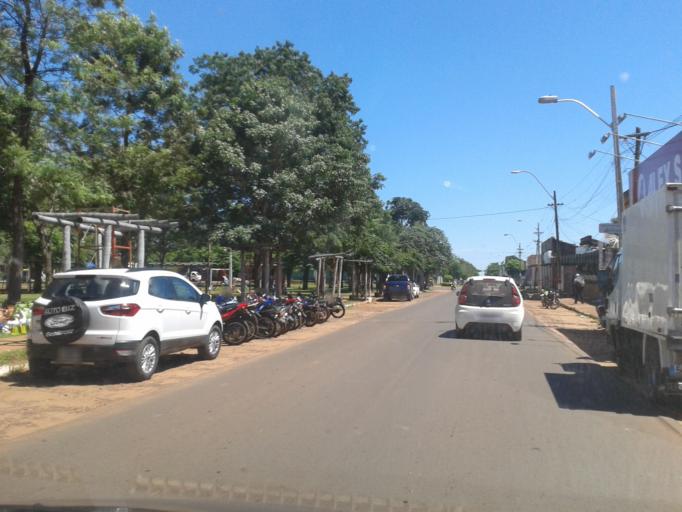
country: PY
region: Misiones
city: Santa Rosa
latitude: -26.8868
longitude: -56.8485
